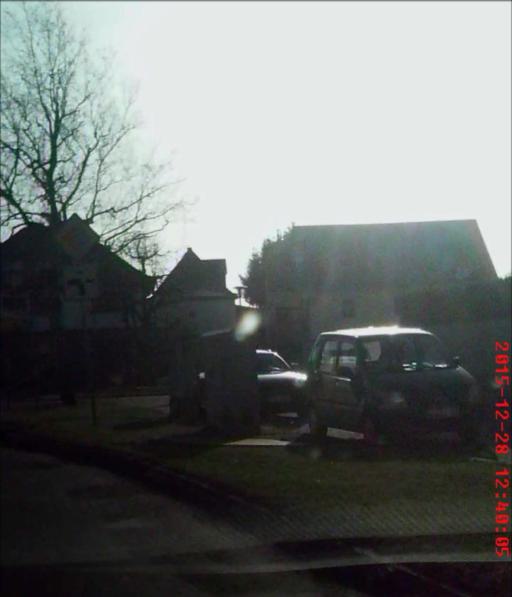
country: DE
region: Thuringia
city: Ossmanstedt
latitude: 51.0114
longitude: 11.4235
